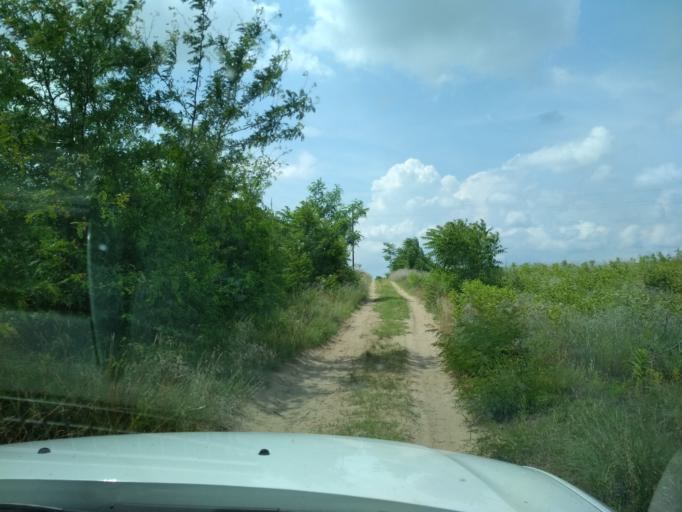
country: HU
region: Pest
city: Tapioszentmarton
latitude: 47.3734
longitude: 19.7620
